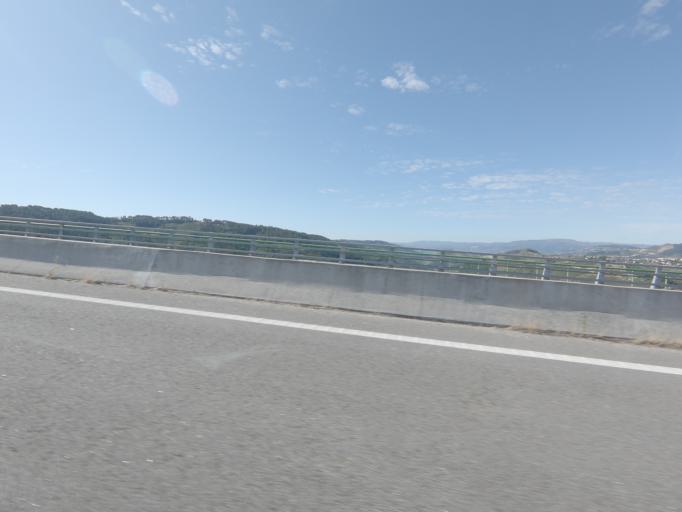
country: PT
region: Vila Real
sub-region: Vila Real
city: Vila Real
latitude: 41.2780
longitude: -7.7457
